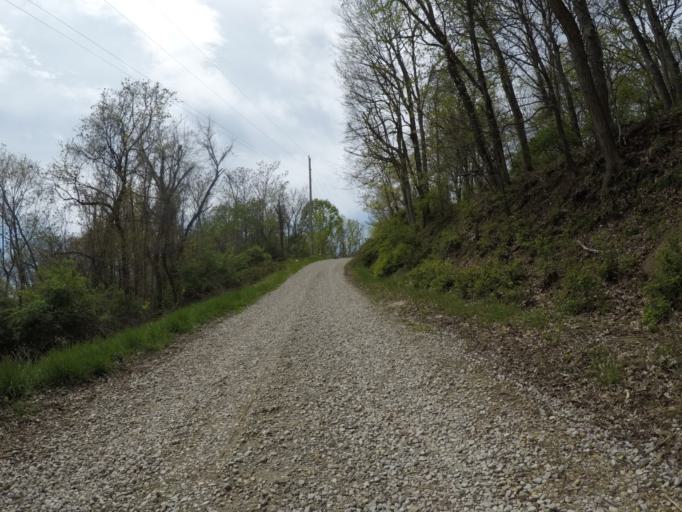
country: US
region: West Virginia
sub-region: Wayne County
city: Lavalette
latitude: 38.3688
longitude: -82.4793
